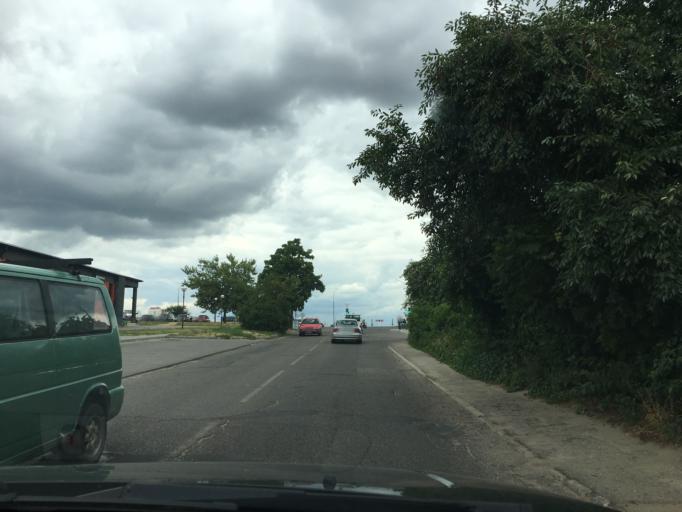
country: BY
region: Grodnenskaya
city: Hrodna
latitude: 53.6291
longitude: 23.8548
